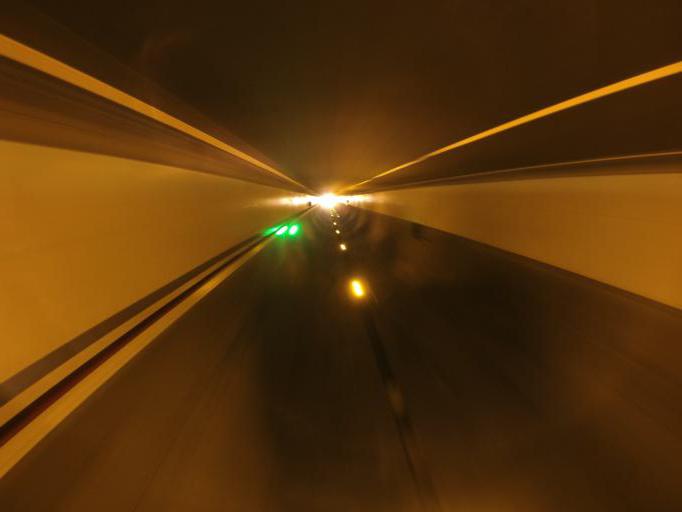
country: PT
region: Madeira
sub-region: Ribeira Brava
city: Campanario
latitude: 32.6955
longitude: -17.0462
